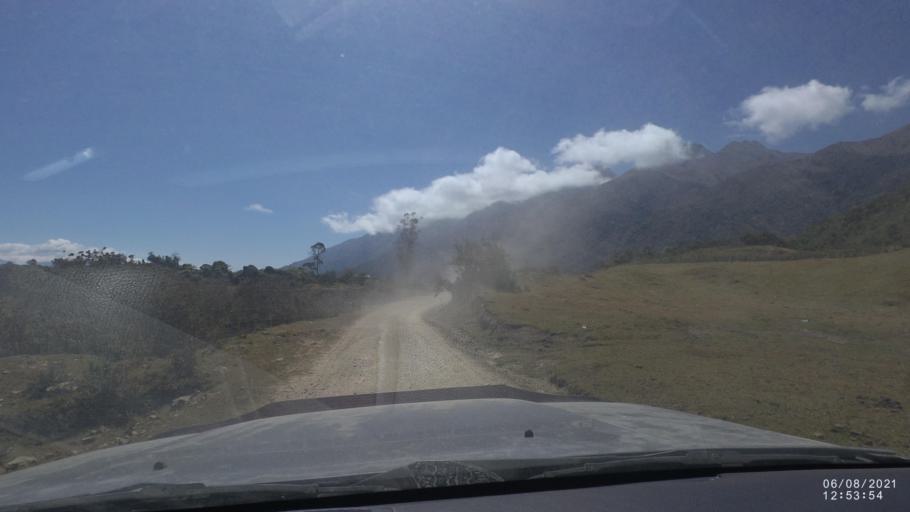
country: BO
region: Cochabamba
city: Colchani
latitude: -16.7611
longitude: -66.6840
